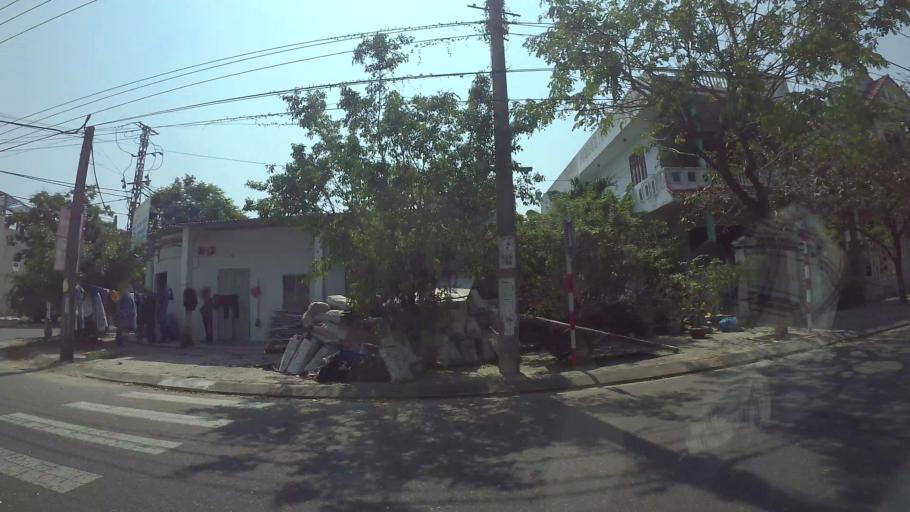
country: VN
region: Da Nang
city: Ngu Hanh Son
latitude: 15.9818
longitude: 108.2733
